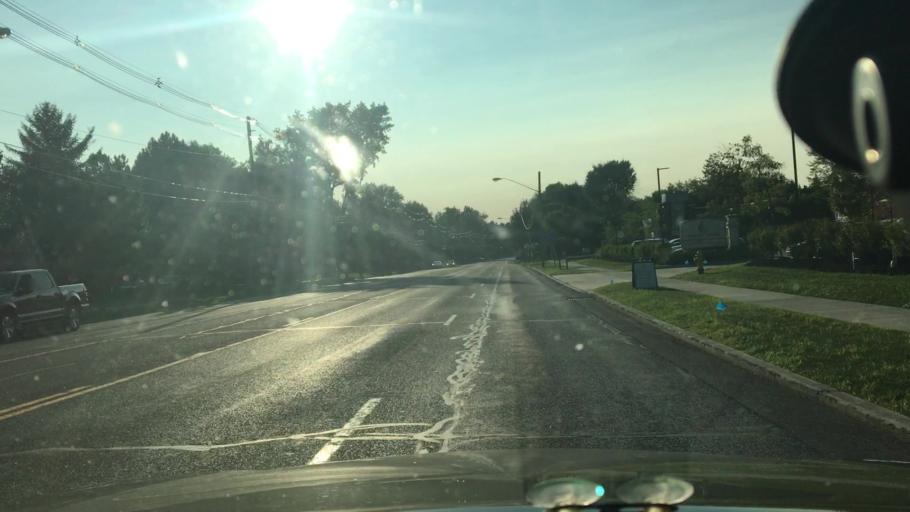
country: US
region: New York
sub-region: Erie County
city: Williamsville
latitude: 42.9594
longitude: -78.7701
